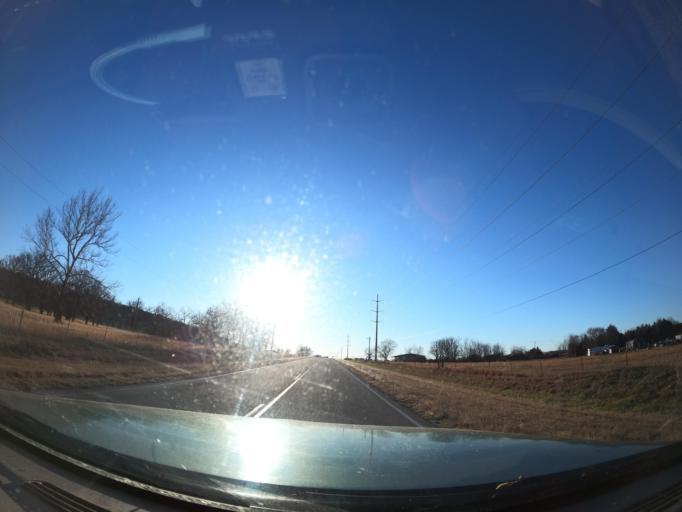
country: US
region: Oklahoma
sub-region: Pittsburg County
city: Hartshorne
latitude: 34.8792
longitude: -95.5024
